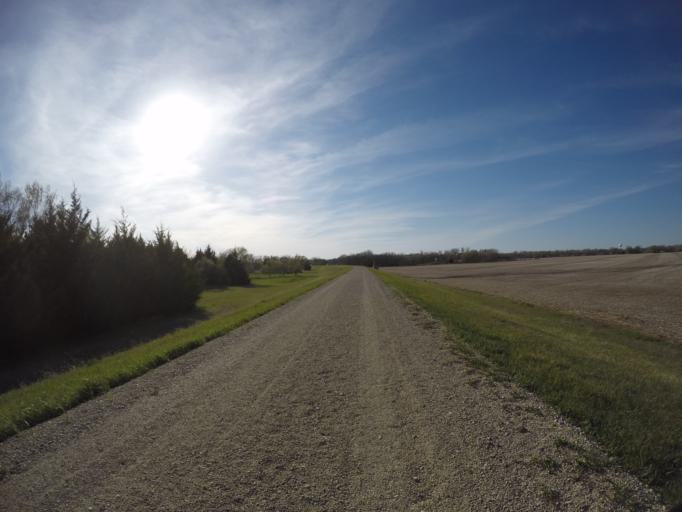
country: US
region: Kansas
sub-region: Saline County
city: Salina
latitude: 38.8642
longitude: -97.6019
